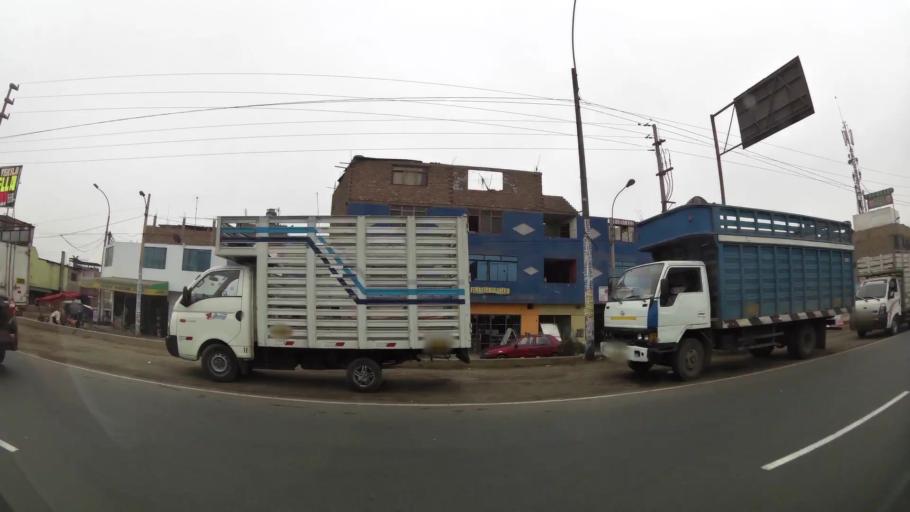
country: PE
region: Lima
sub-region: Lima
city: Urb. Santo Domingo
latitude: -11.9157
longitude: -77.0408
